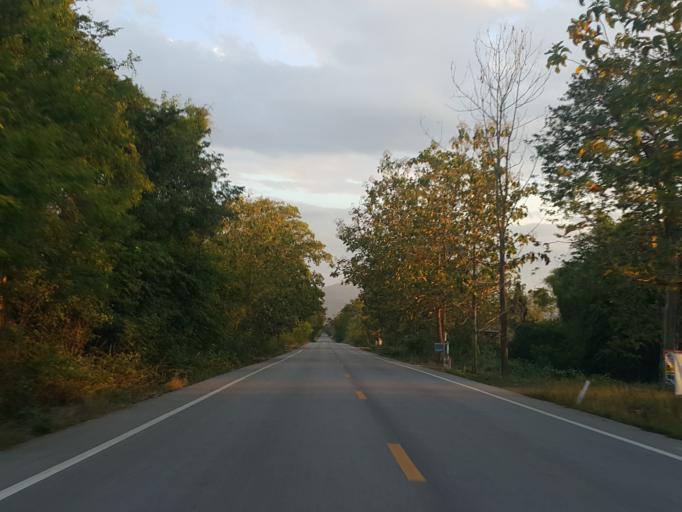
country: TH
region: Lampang
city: Mae Mo
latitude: 18.4405
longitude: 99.6387
